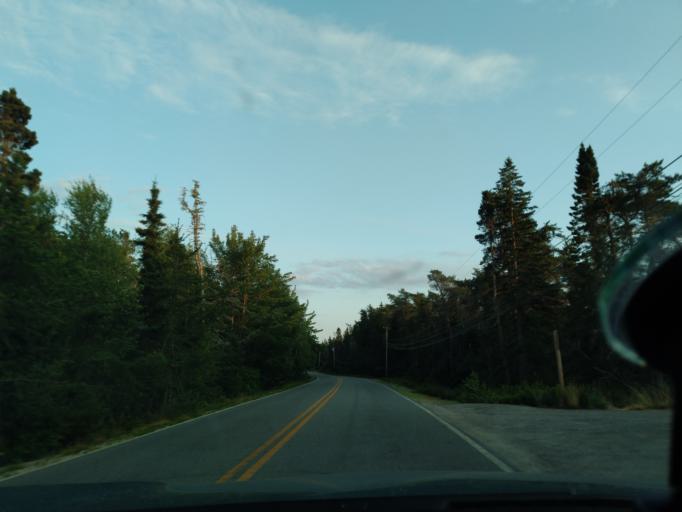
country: US
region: Maine
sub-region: Hancock County
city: Gouldsboro
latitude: 44.3784
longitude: -68.0363
